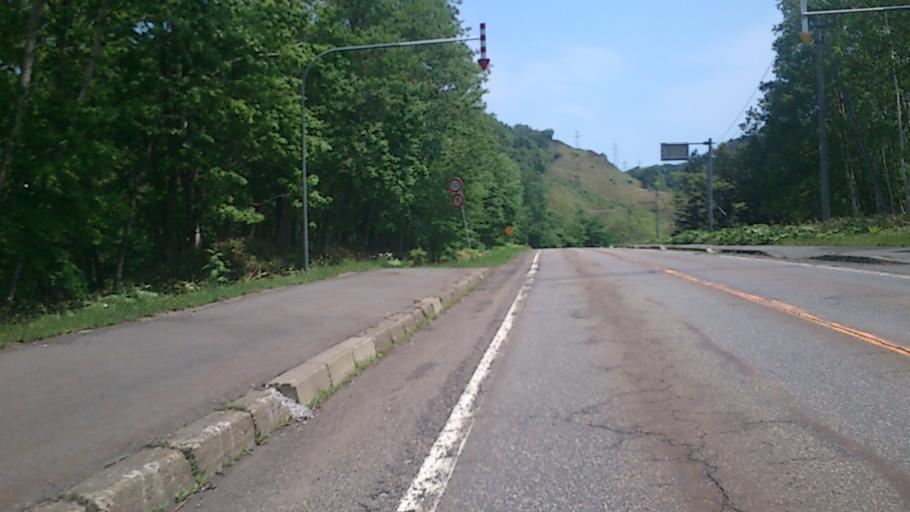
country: JP
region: Hokkaido
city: Otofuke
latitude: 43.3602
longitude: 143.2497
